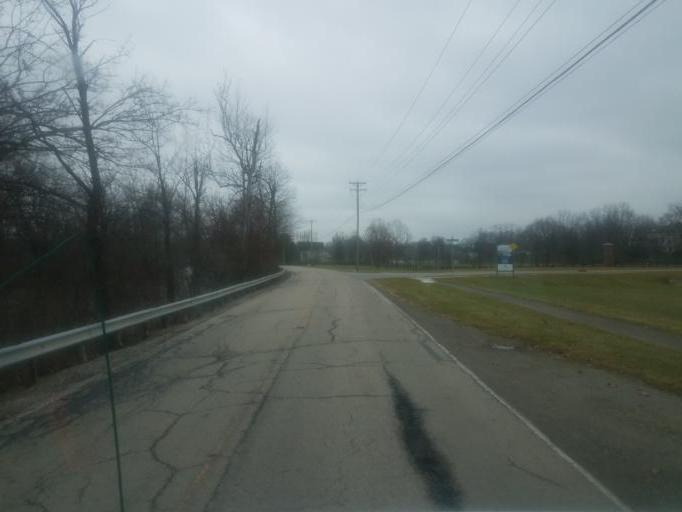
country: US
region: Ohio
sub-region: Franklin County
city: Westerville
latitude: 40.1321
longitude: -82.9504
